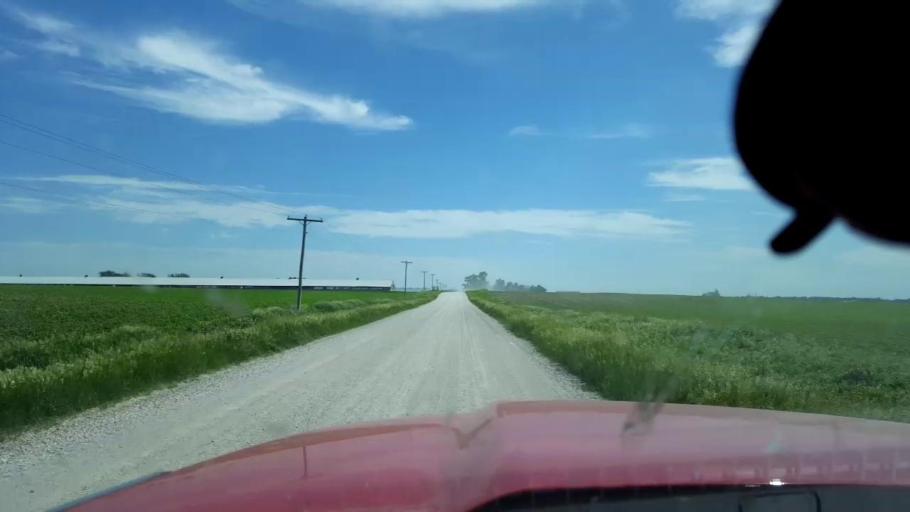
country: US
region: Iowa
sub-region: Hamilton County
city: Jewell
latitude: 42.3456
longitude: -93.5603
